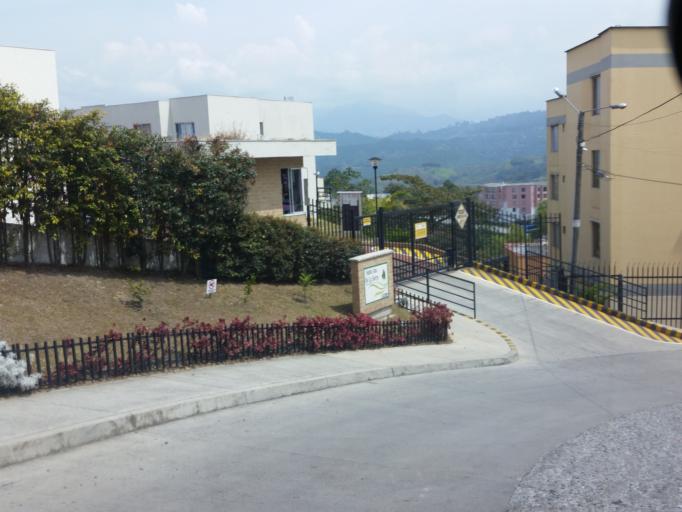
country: CO
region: Caldas
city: Manizales
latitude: 5.0869
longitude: -75.5284
